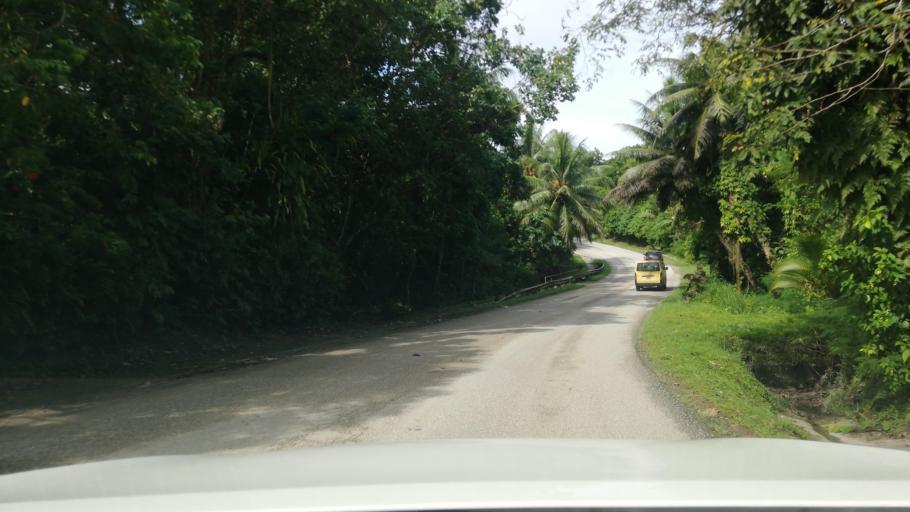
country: FM
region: Yap
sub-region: Weloy Municipality
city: Colonia
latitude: 9.5147
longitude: 138.1093
